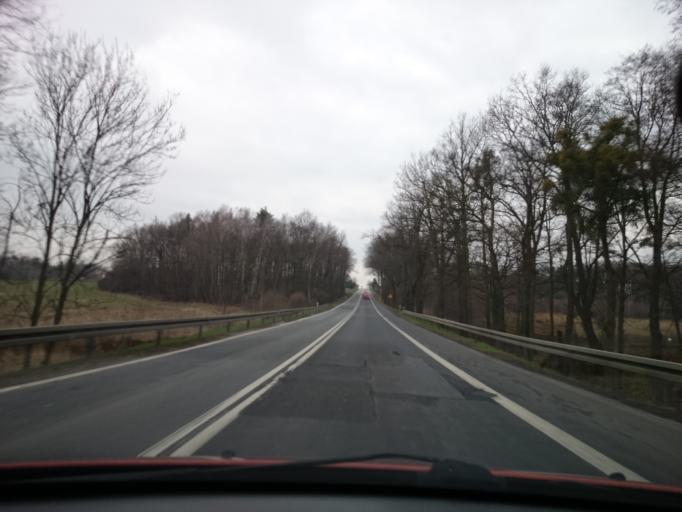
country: PL
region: Opole Voivodeship
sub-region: Powiat opolski
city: Niemodlin
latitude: 50.6320
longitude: 17.5912
